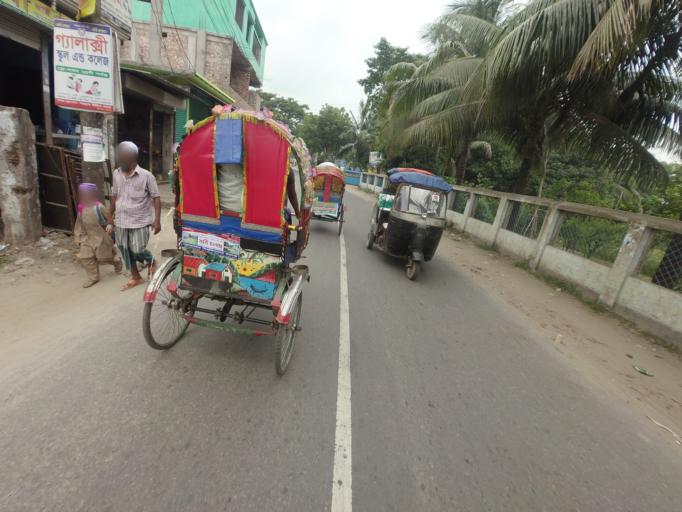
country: BD
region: Dhaka
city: Azimpur
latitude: 23.7288
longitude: 90.3383
